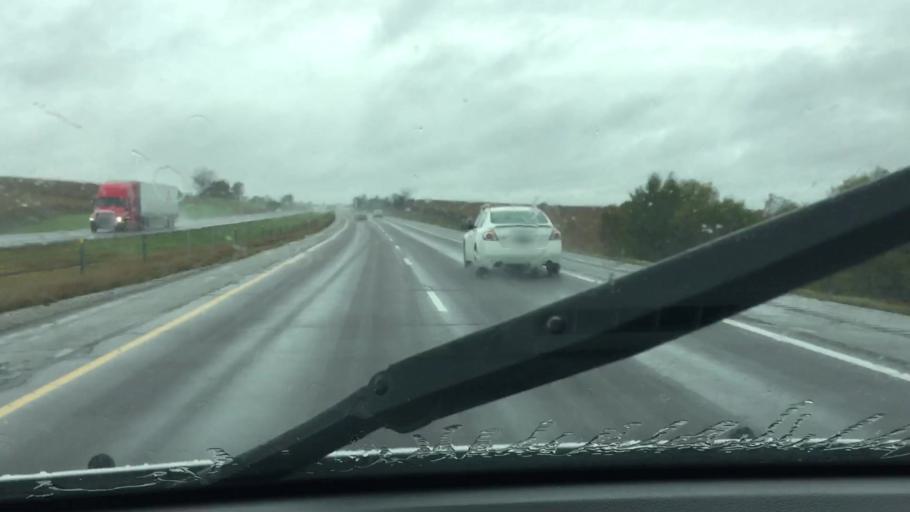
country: US
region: Iowa
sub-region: Poweshiek County
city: Brooklyn
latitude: 41.6964
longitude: -92.5320
